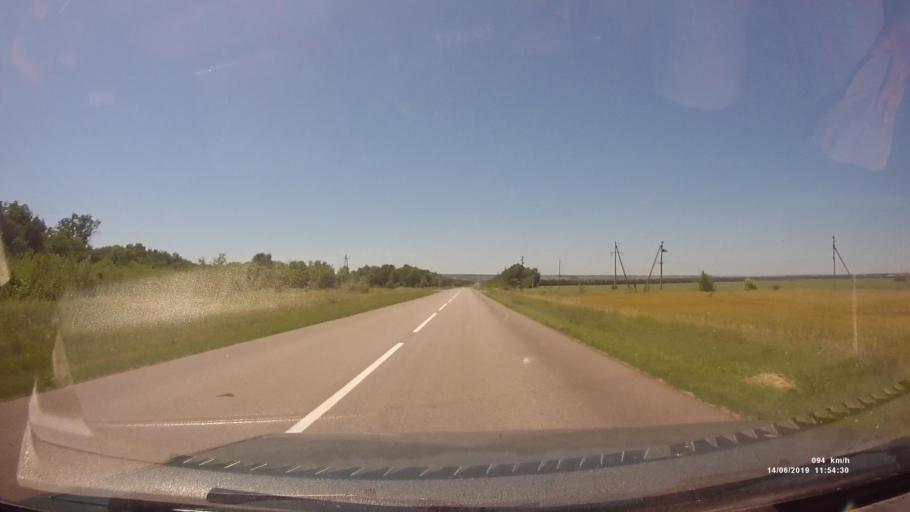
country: RU
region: Rostov
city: Kazanskaya
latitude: 49.8184
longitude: 41.1932
